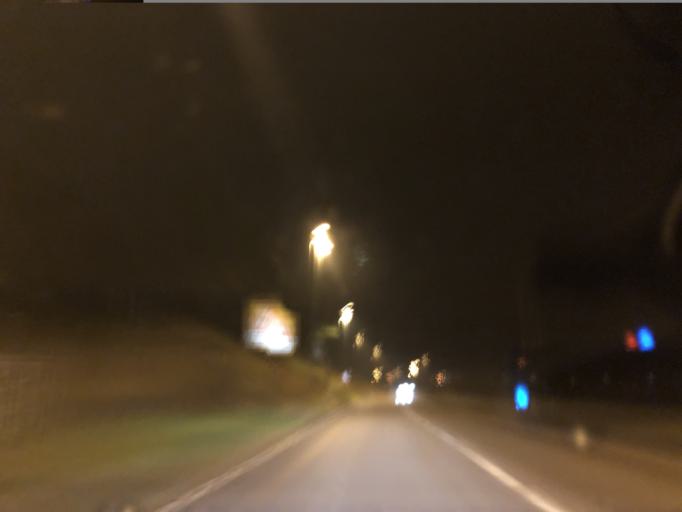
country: GB
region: England
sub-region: Borough of Oldham
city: Shaw
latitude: 53.5786
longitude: -2.0535
